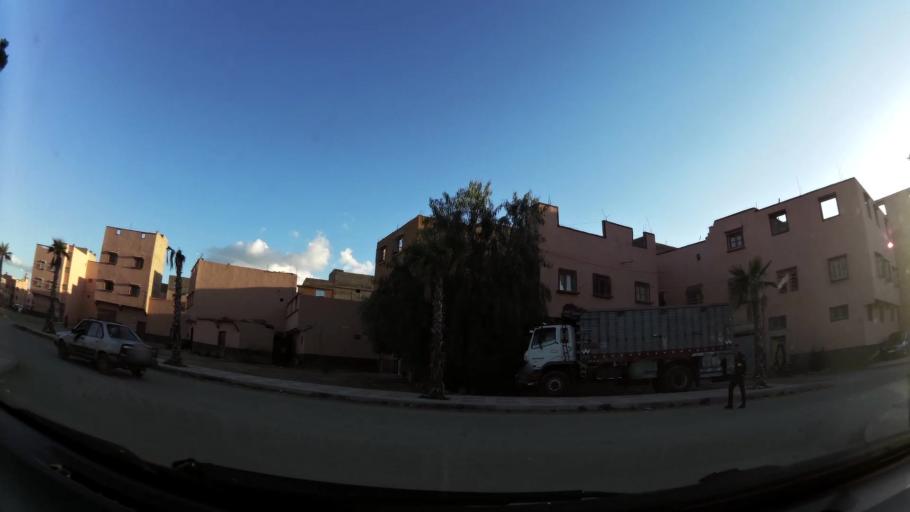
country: MA
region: Marrakech-Tensift-Al Haouz
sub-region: Kelaa-Des-Sraghna
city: Sidi Abdallah
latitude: 32.2460
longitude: -7.9492
